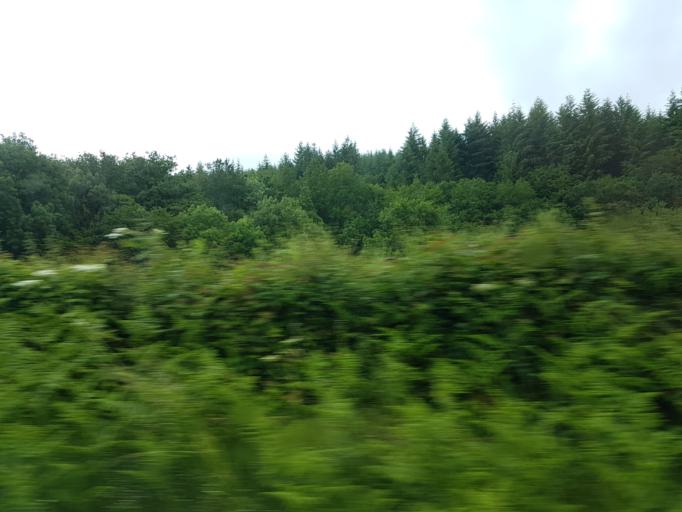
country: FR
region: Bourgogne
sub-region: Departement de la Nievre
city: Lormes
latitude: 47.1838
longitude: 3.8113
